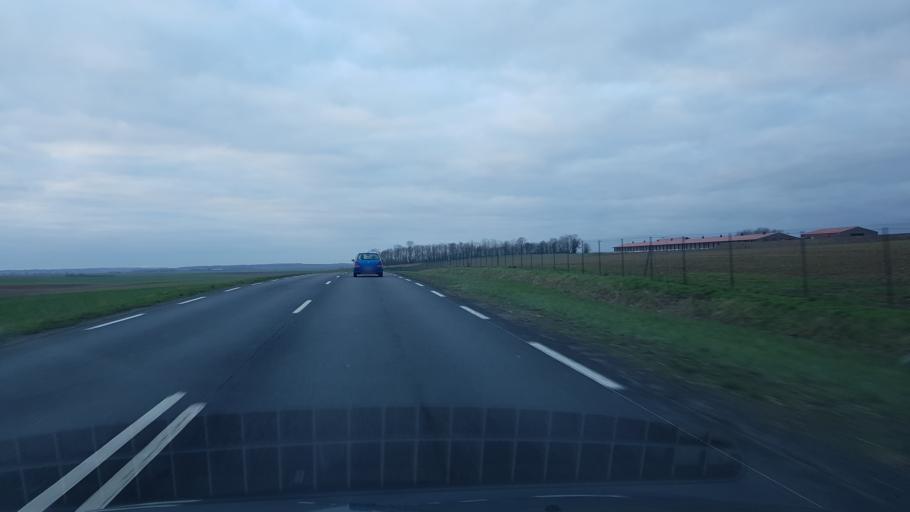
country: FR
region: Ile-de-France
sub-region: Departement de Seine-et-Marne
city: Villiers-Saint-Georges
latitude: 48.6936
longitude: 3.4194
